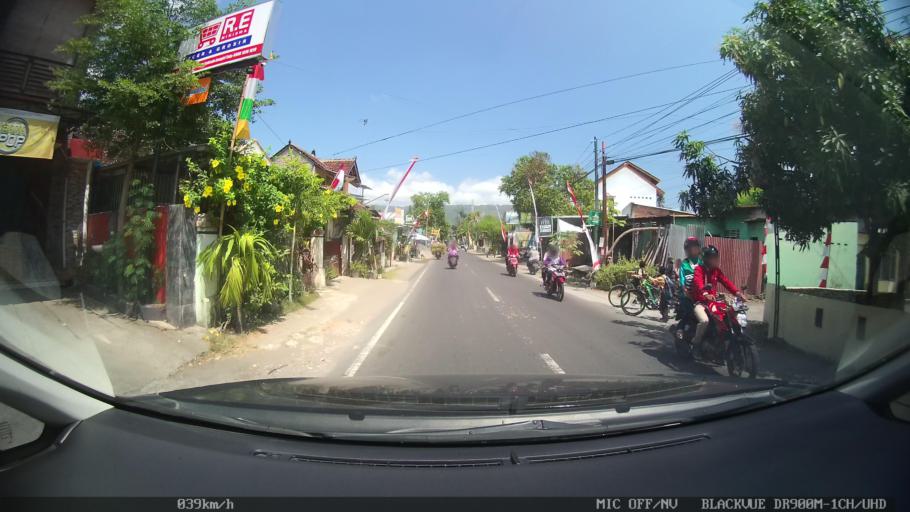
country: ID
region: Daerah Istimewa Yogyakarta
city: Pundong
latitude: -7.9372
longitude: 110.3739
